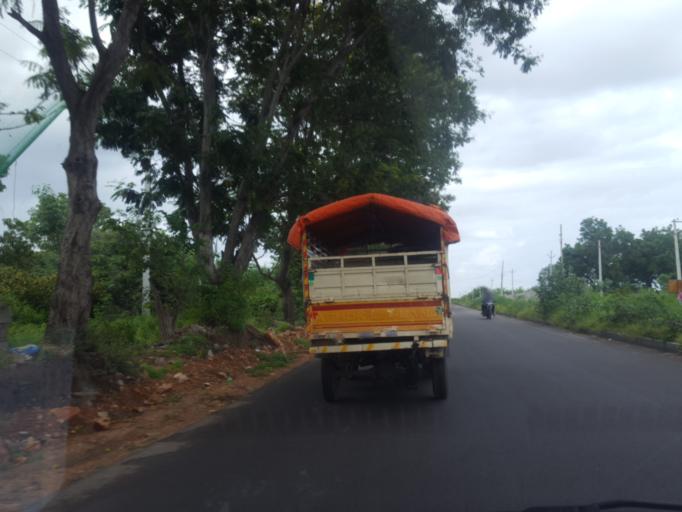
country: IN
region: Telangana
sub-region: Medak
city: Serilingampalle
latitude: 17.4105
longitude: 78.2722
